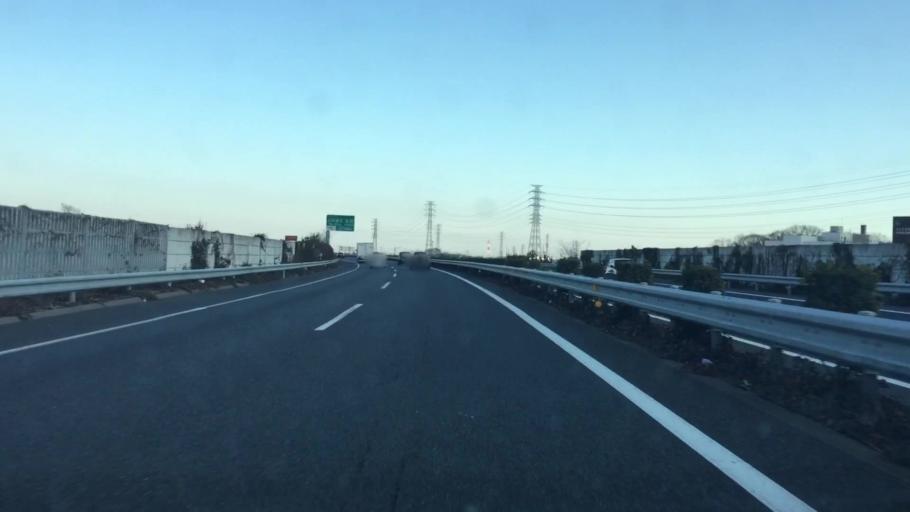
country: JP
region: Gunma
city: Ota
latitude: 36.3311
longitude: 139.3786
